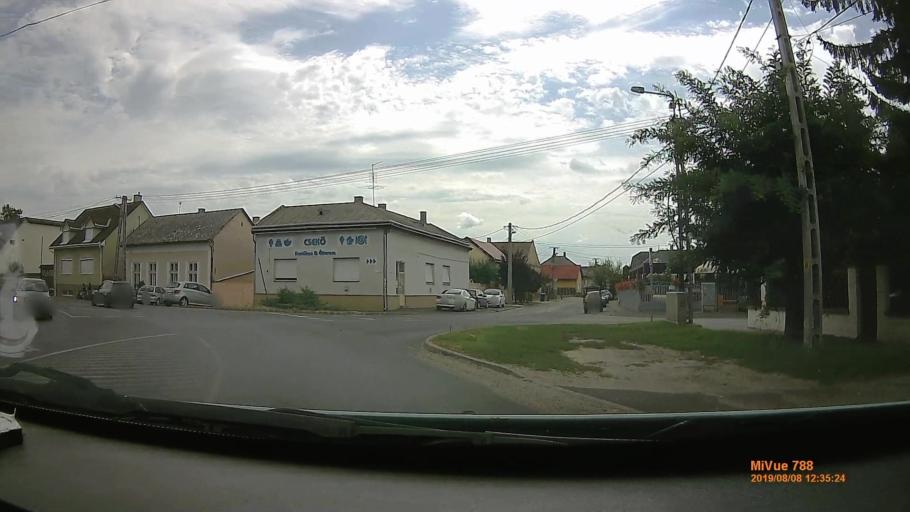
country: HU
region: Szabolcs-Szatmar-Bereg
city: Nyirbator
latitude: 47.8351
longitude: 22.1269
